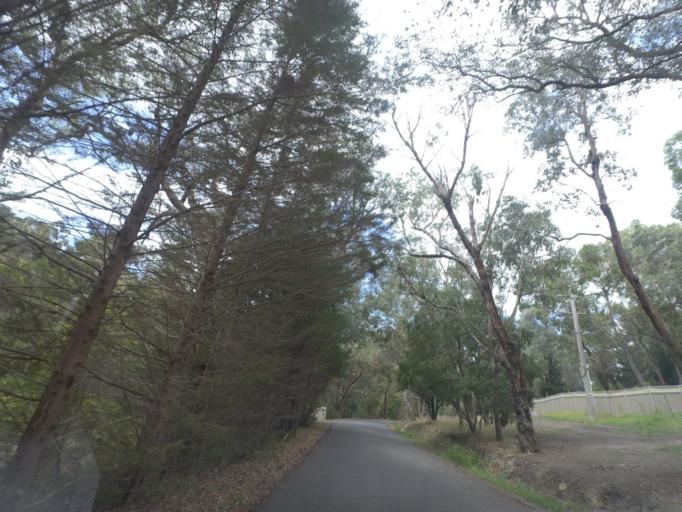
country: AU
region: Victoria
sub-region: Manningham
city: Park Orchards
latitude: -37.7919
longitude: 145.2102
